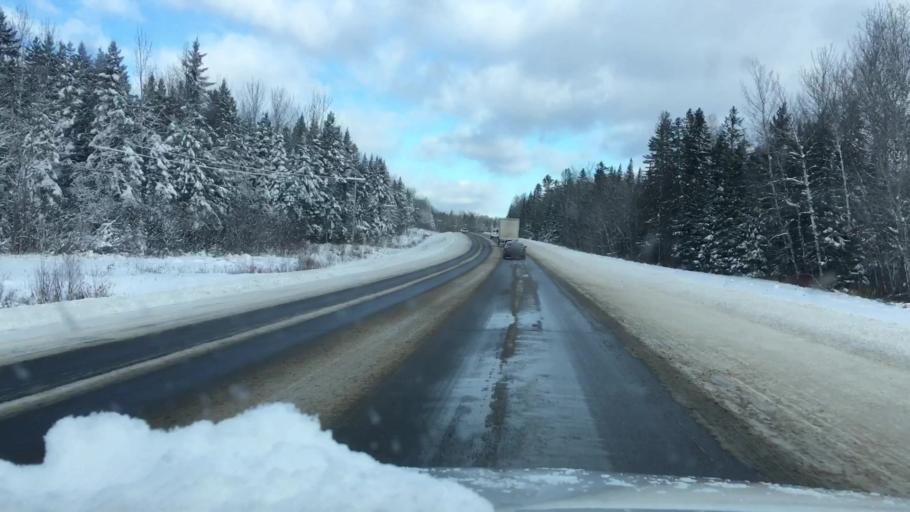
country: US
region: Maine
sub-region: Aroostook County
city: Caribou
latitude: 46.8340
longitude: -67.9972
